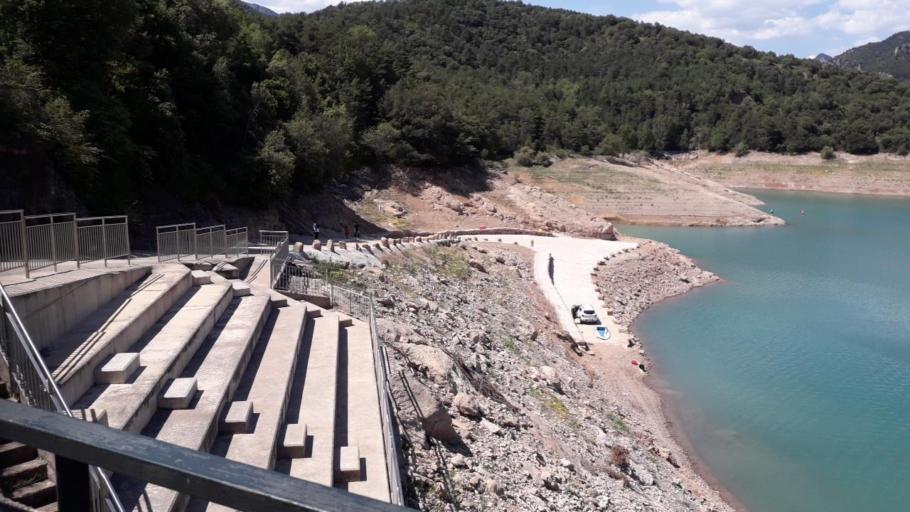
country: ES
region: Catalonia
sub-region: Provincia de Barcelona
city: Berga
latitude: 42.1220
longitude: 1.8763
